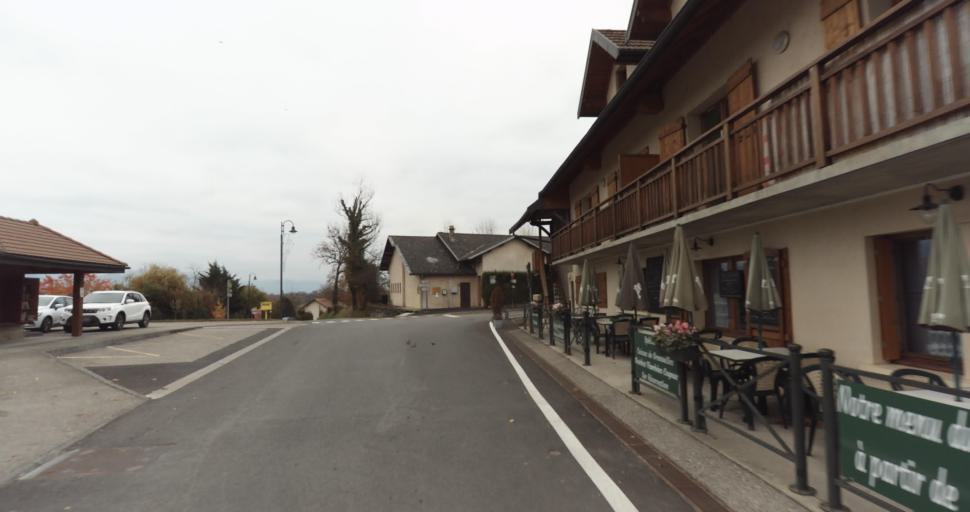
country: FR
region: Rhone-Alpes
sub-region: Departement de la Haute-Savoie
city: Chavanod
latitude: 45.8611
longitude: 6.0444
